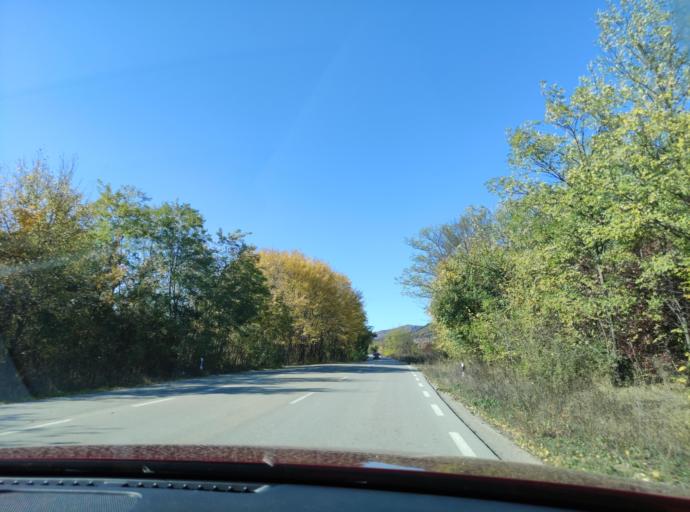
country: BG
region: Montana
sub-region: Obshtina Chiprovtsi
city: Chiprovtsi
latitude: 43.4261
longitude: 23.0076
